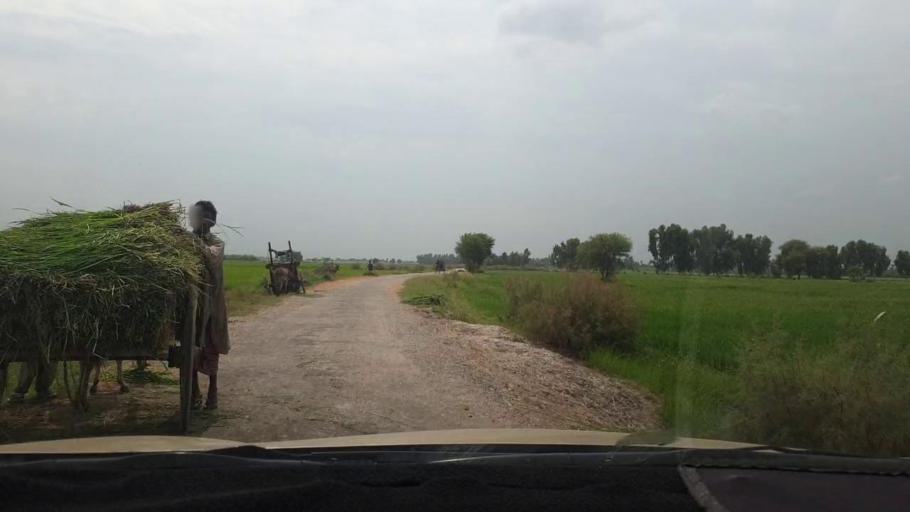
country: PK
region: Sindh
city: Naudero
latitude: 27.6271
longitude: 68.3202
